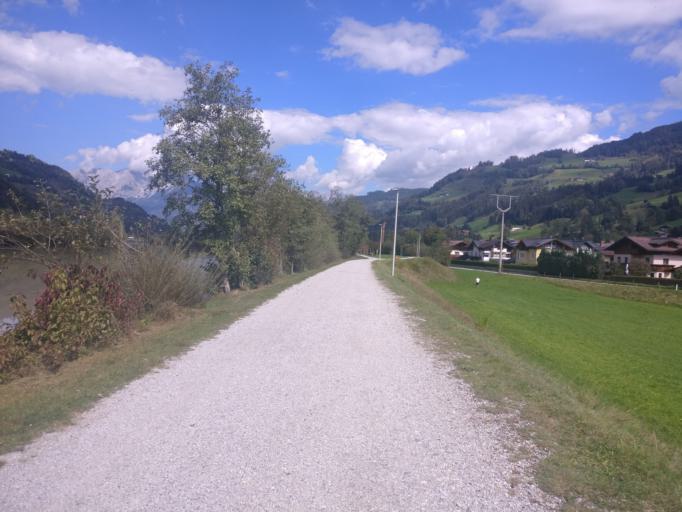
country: AT
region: Salzburg
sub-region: Politischer Bezirk Sankt Johann im Pongau
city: Sankt Johann im Pongau
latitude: 47.3670
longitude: 13.2091
